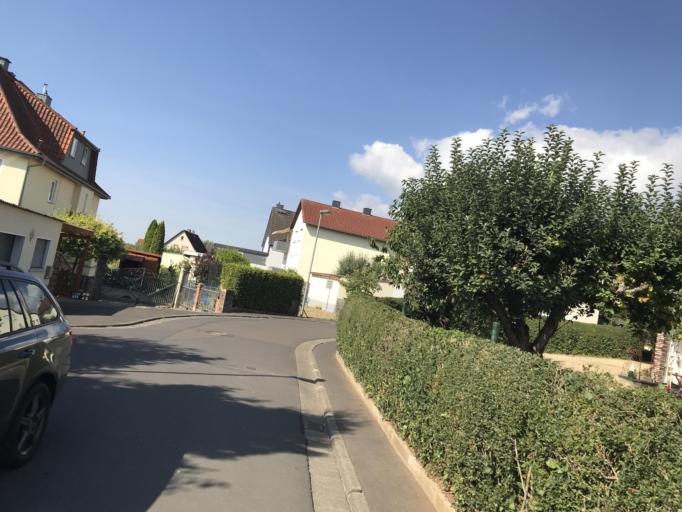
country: DE
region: Hesse
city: Staufenberg
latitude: 50.6628
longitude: 8.7470
